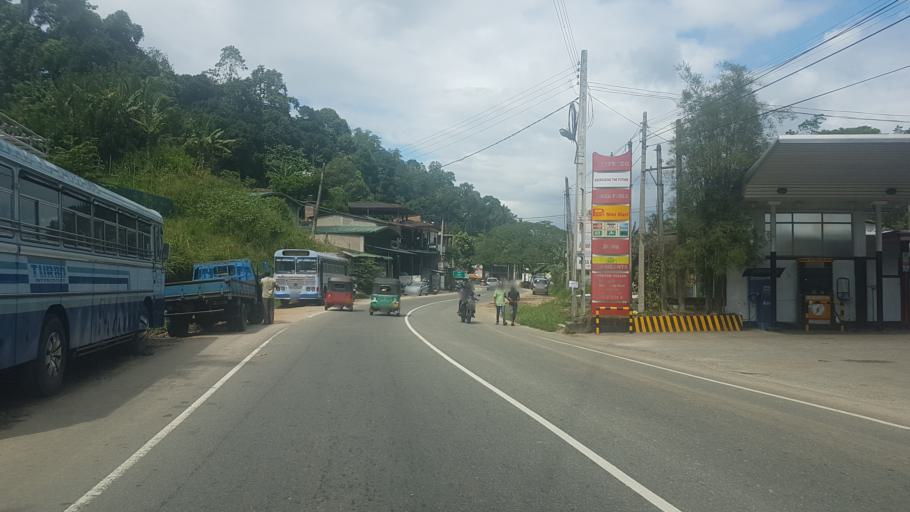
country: LK
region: Central
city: Gampola
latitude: 7.2091
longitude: 80.5988
